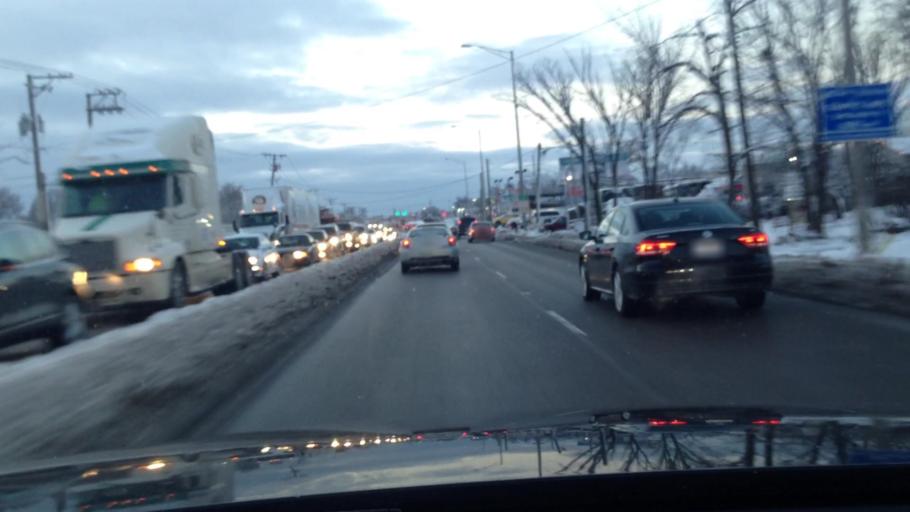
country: US
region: Illinois
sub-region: Lake County
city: Kildeer
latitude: 42.1542
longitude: -88.0391
